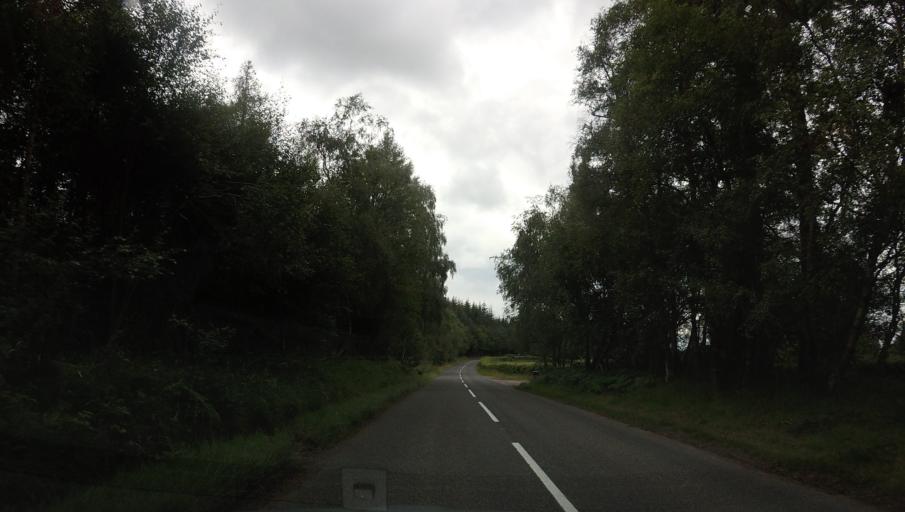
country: GB
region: Scotland
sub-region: Aberdeenshire
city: Torphins
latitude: 57.0636
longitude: -2.6874
